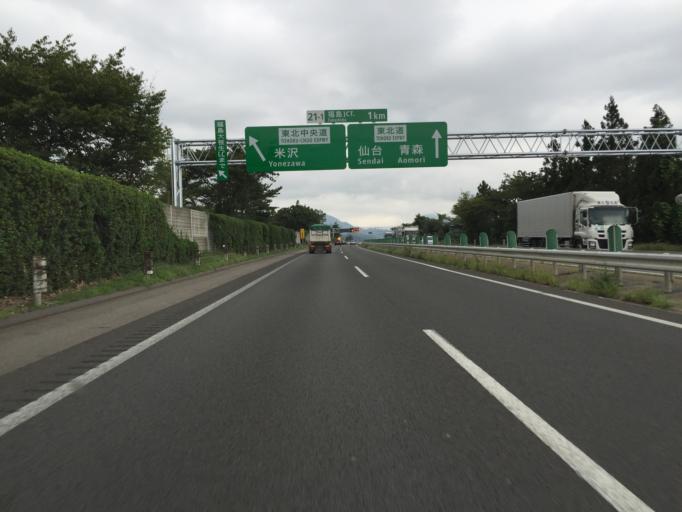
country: JP
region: Fukushima
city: Fukushima-shi
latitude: 37.7794
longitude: 140.4133
